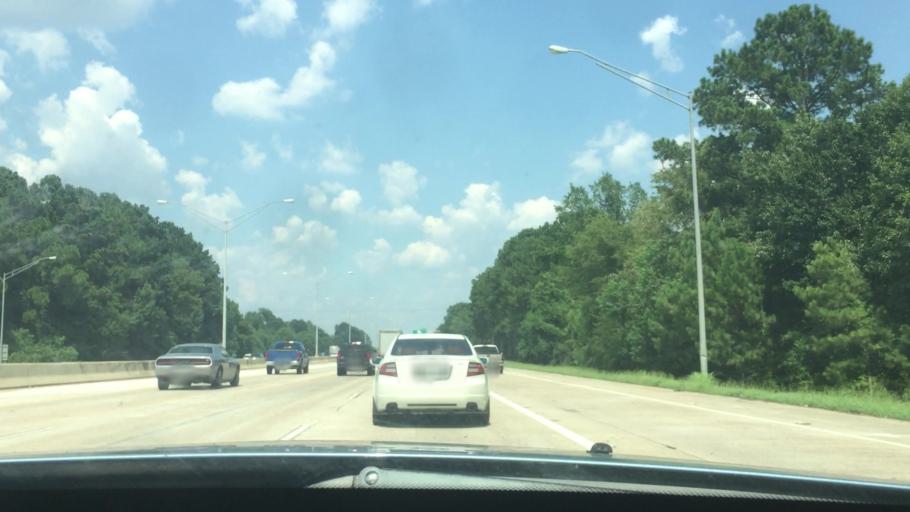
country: US
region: Louisiana
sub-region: East Baton Rouge Parish
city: Shenandoah
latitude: 30.4391
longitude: -91.0201
